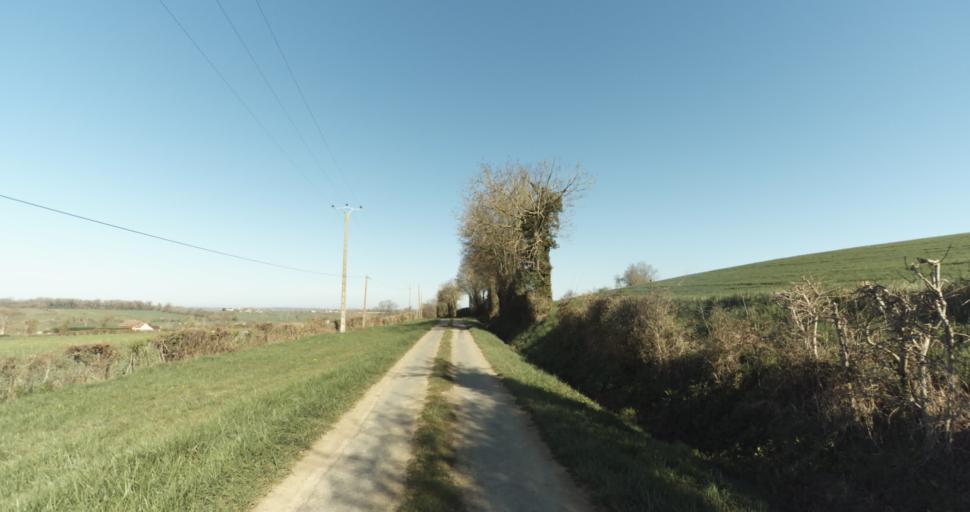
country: FR
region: Lower Normandy
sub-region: Departement du Calvados
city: Saint-Pierre-sur-Dives
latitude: 48.9839
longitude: 0.0175
